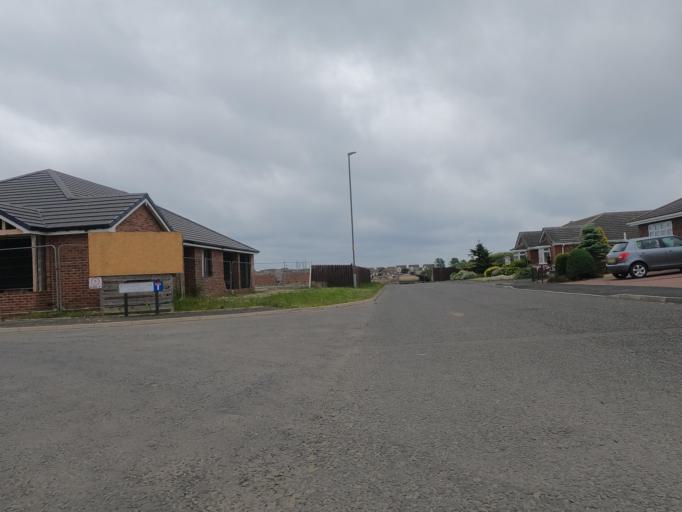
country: GB
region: England
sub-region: Northumberland
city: Blyth
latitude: 55.1085
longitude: -1.5225
